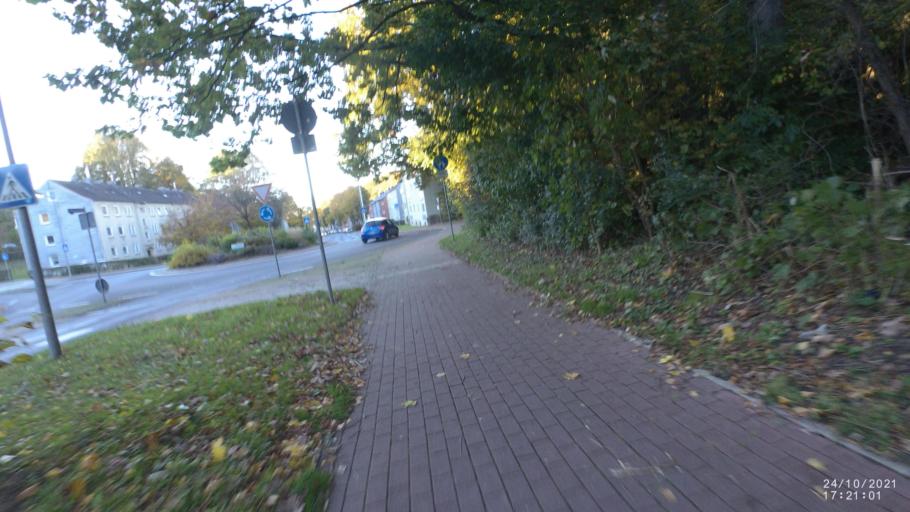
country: DE
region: North Rhine-Westphalia
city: Iserlohn
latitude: 51.3787
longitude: 7.7272
